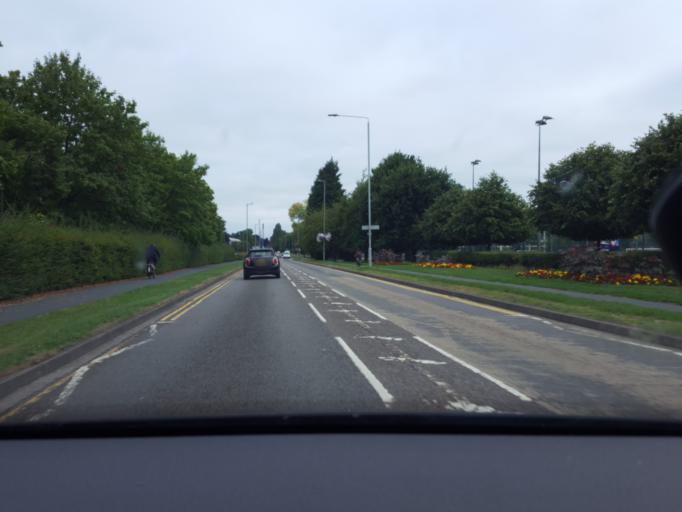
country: GB
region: England
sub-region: Leicestershire
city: Loughborough
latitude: 52.7655
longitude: -1.2197
